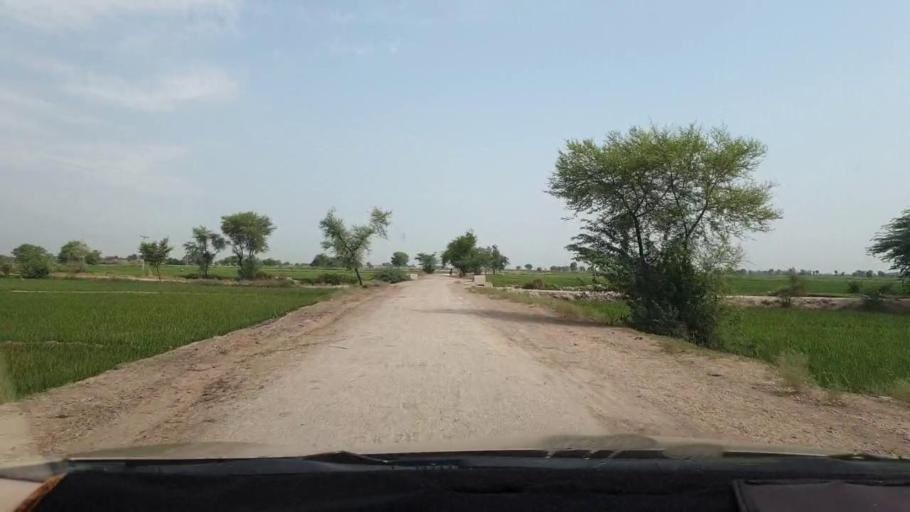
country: PK
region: Sindh
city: Larkana
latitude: 27.6750
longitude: 68.2202
